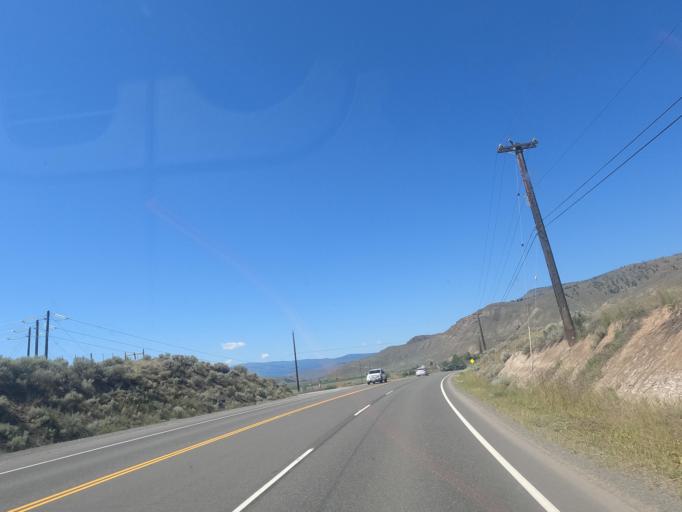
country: CA
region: British Columbia
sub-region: Thompson-Nicola Regional District
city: Ashcroft
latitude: 50.7978
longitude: -121.1199
